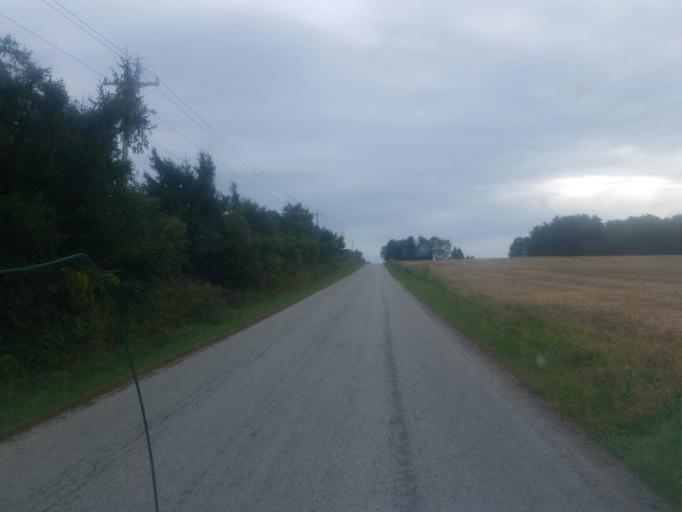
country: US
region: Ohio
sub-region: Crawford County
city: Galion
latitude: 40.6391
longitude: -82.7531
